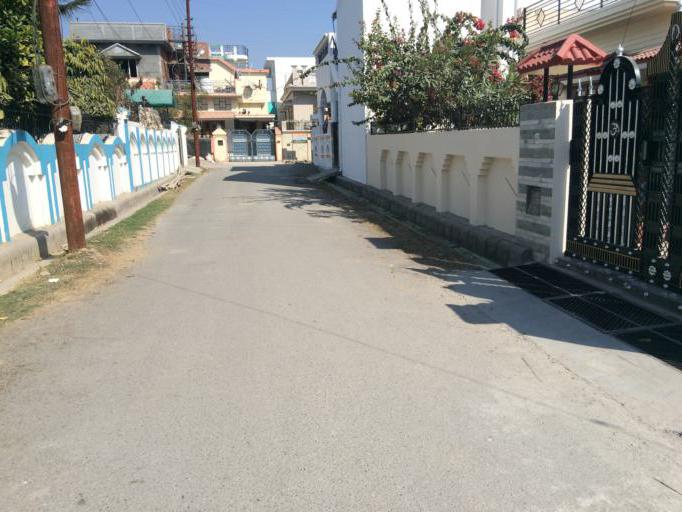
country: IN
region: Uttarakhand
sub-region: Dehradun
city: Raipur
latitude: 30.2869
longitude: 78.0578
